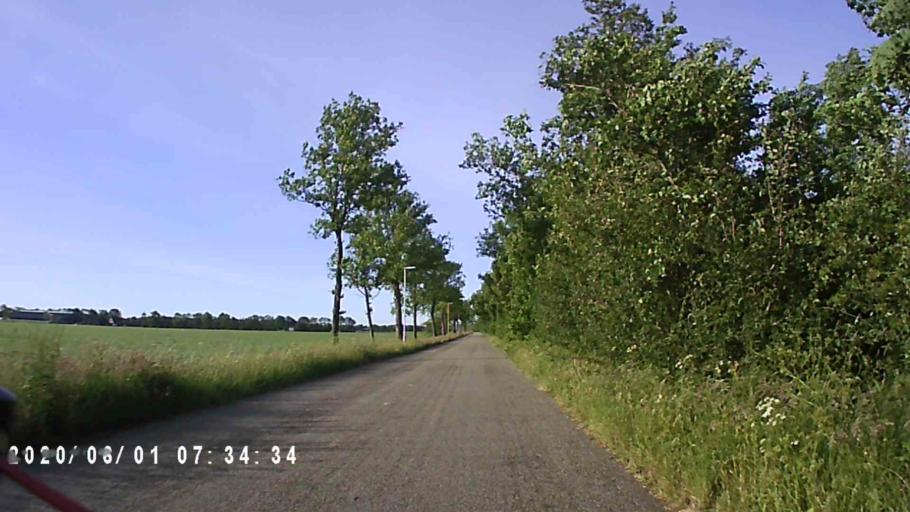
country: NL
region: Friesland
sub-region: Gemeente Dongeradeel
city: Dokkum
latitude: 53.3094
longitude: 5.9943
